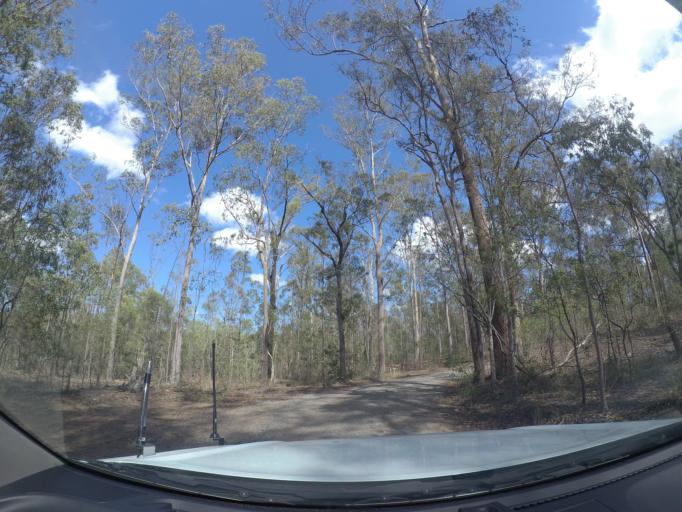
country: AU
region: Queensland
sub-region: Logan
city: Cedar Vale
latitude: -27.8374
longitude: 152.9667
